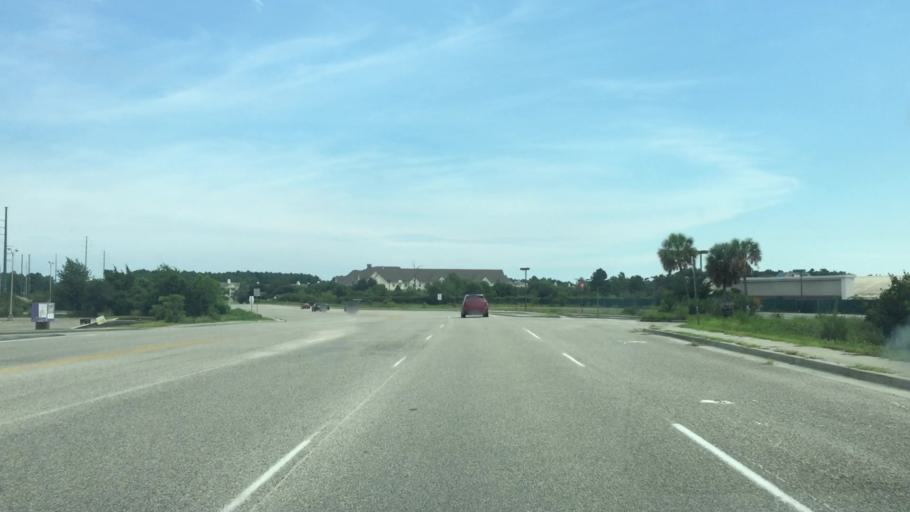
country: US
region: South Carolina
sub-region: Horry County
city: Forestbrook
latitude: 33.7172
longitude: -78.9311
